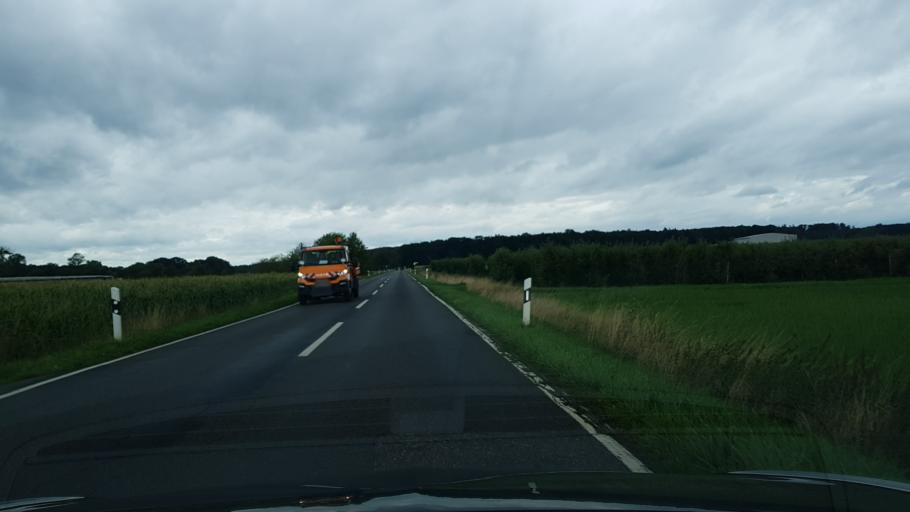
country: DE
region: North Rhine-Westphalia
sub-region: Regierungsbezirk Koln
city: Wachtberg
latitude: 50.6118
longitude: 7.0778
